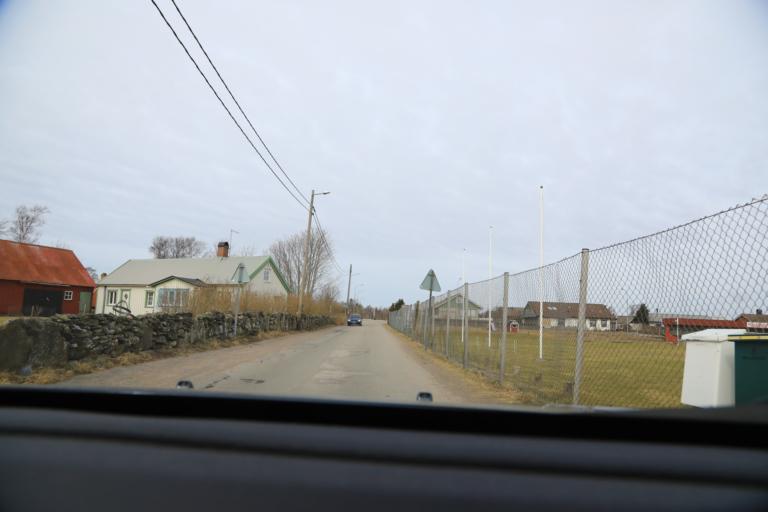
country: SE
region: Halland
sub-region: Kungsbacka Kommun
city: Frillesas
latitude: 57.2303
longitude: 12.1244
